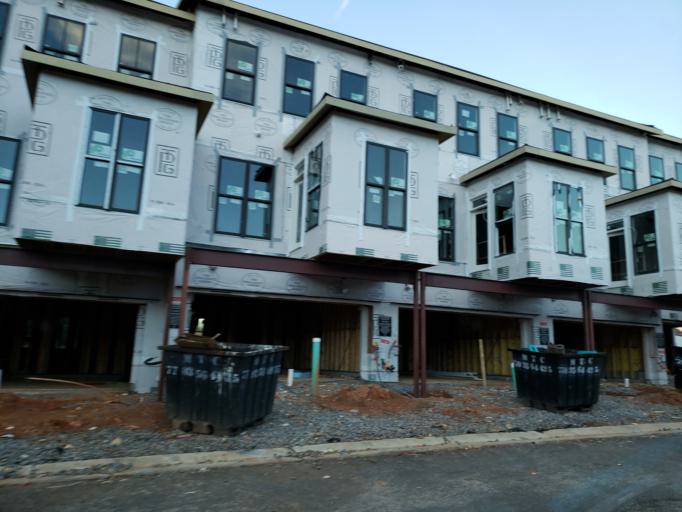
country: US
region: Georgia
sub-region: Fulton County
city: Alpharetta
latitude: 34.0694
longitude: -84.2899
